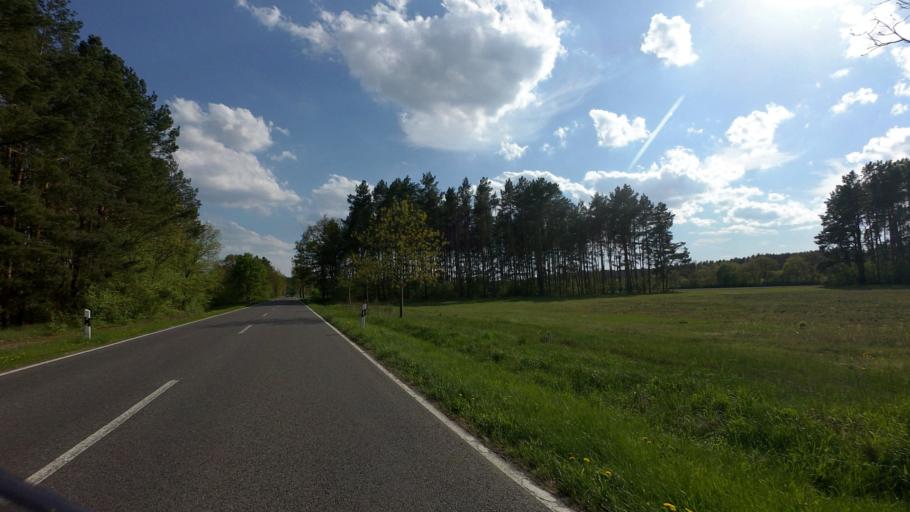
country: DE
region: Brandenburg
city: Liebenwalde
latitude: 52.9350
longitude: 13.3903
